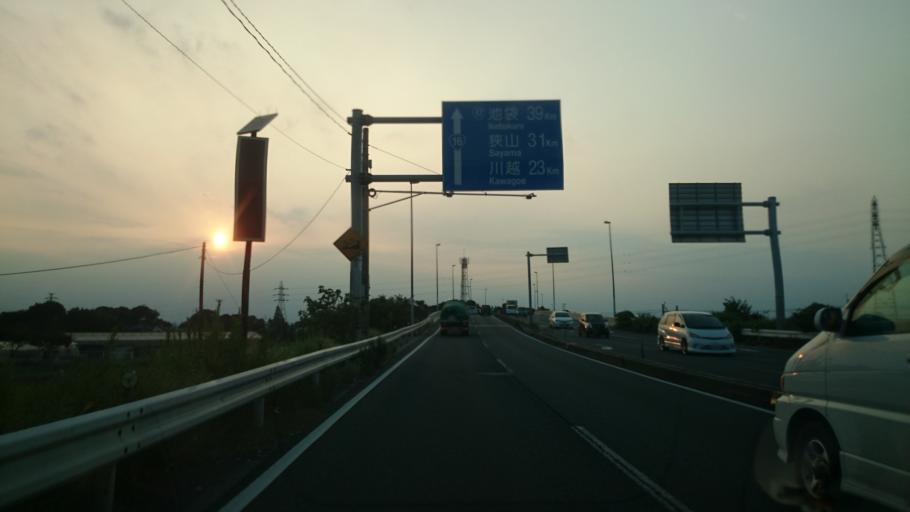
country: JP
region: Saitama
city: Iwatsuki
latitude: 35.9407
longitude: 139.6799
